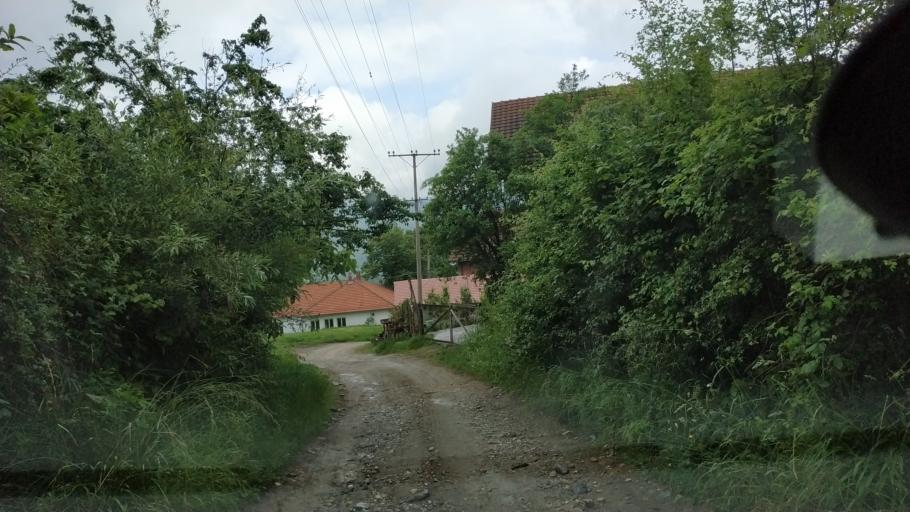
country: RS
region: Central Serbia
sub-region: Toplicki Okrug
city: Prokuplje
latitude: 43.4004
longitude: 21.5488
